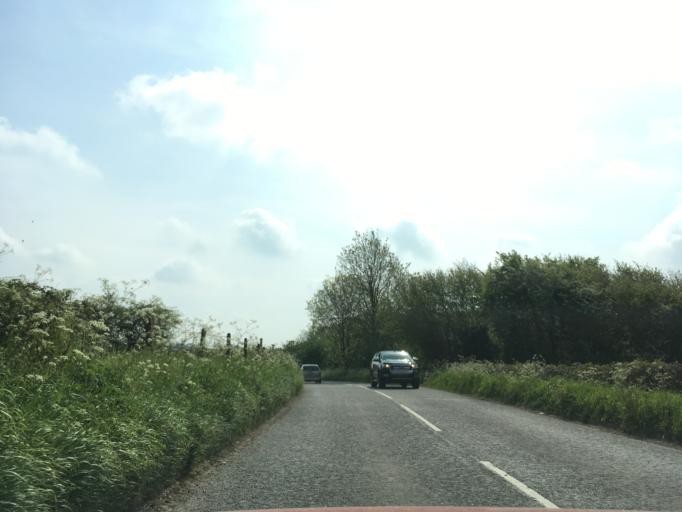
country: GB
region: England
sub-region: North Somerset
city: Winford
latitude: 51.3851
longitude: -2.6767
